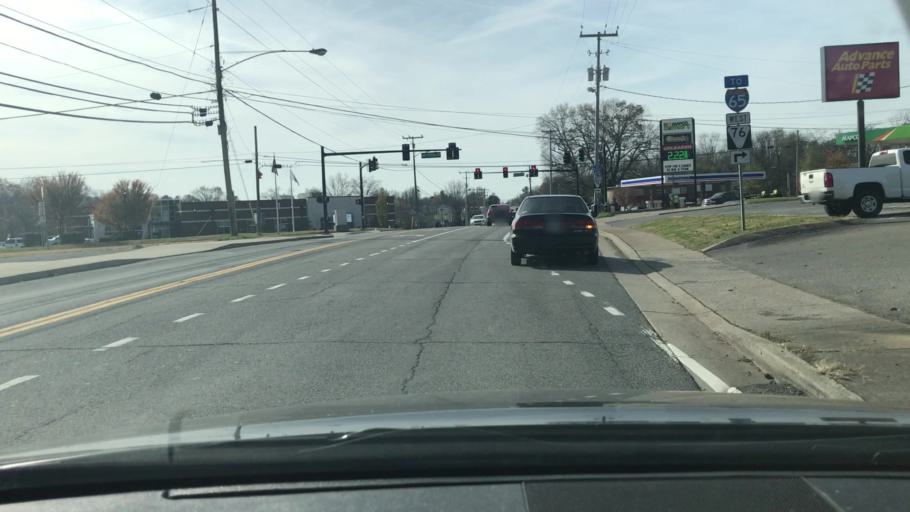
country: US
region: Tennessee
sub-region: Sumner County
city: White House
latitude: 36.4690
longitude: -86.6529
